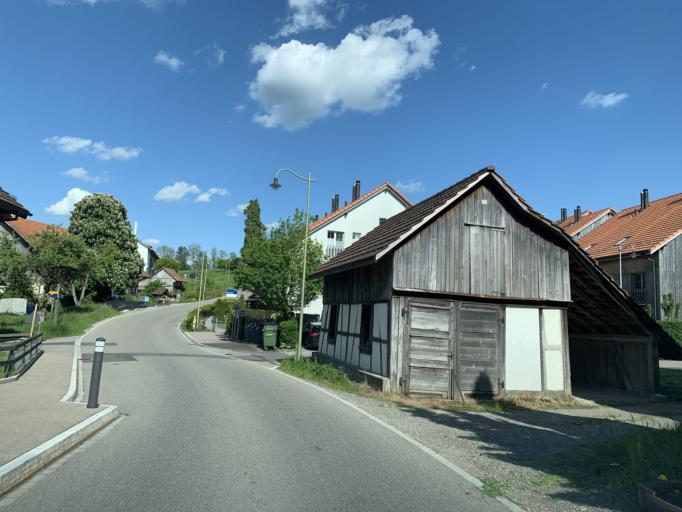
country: CH
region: Zurich
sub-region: Bezirk Pfaeffikon
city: Weisslingen
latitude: 47.4489
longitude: 8.7374
